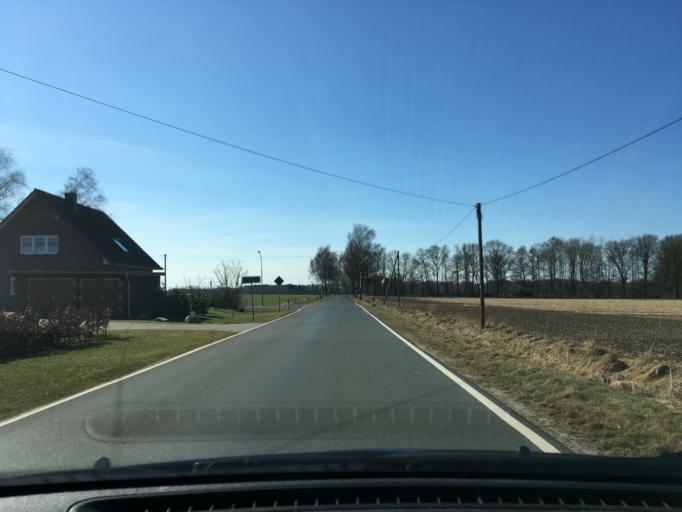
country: DE
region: Lower Saxony
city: Neuenkirchen
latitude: 53.0787
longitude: 9.7209
